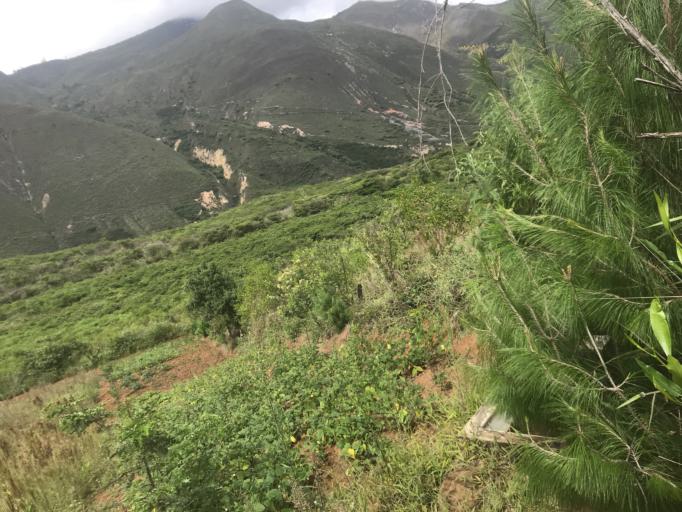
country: PE
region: Amazonas
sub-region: Provincia de Chachapoyas
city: Magdalena
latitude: -6.4018
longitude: -77.8845
